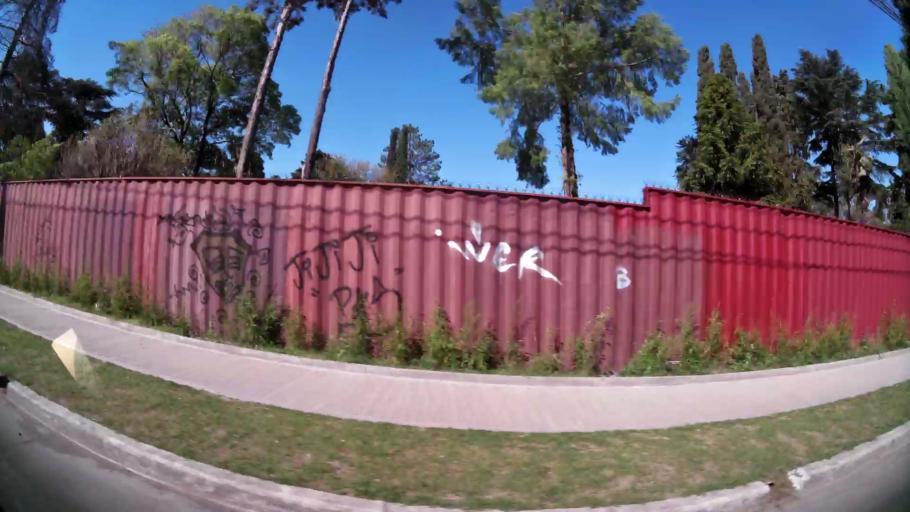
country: AR
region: Buenos Aires
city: Santa Catalina - Dique Lujan
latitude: -34.4864
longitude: -58.6955
